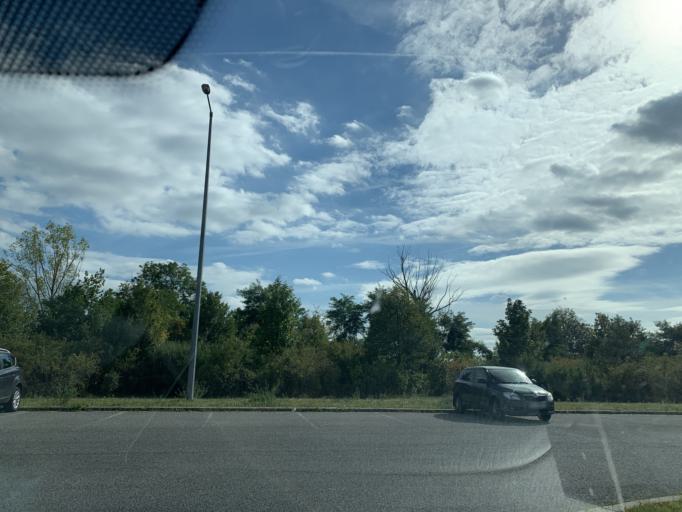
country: SK
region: Trenciansky
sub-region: Okres Nove Mesto nad Vahom
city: Nove Mesto nad Vahom
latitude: 48.7654
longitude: 17.8847
